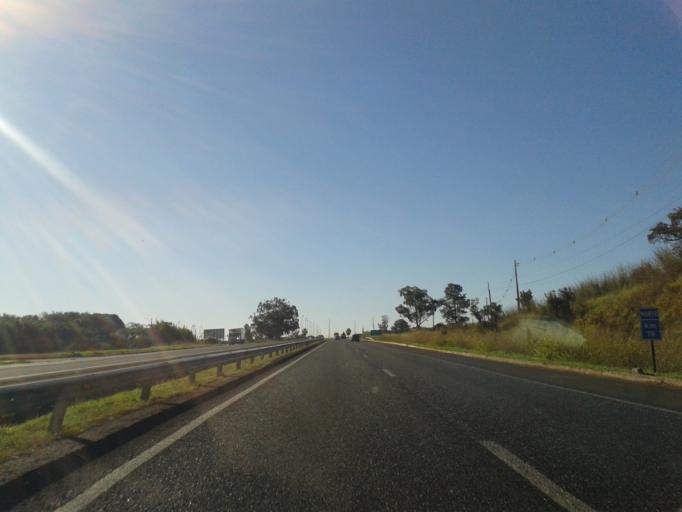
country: BR
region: Minas Gerais
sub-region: Uberlandia
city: Uberlandia
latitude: -18.9446
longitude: -48.2184
